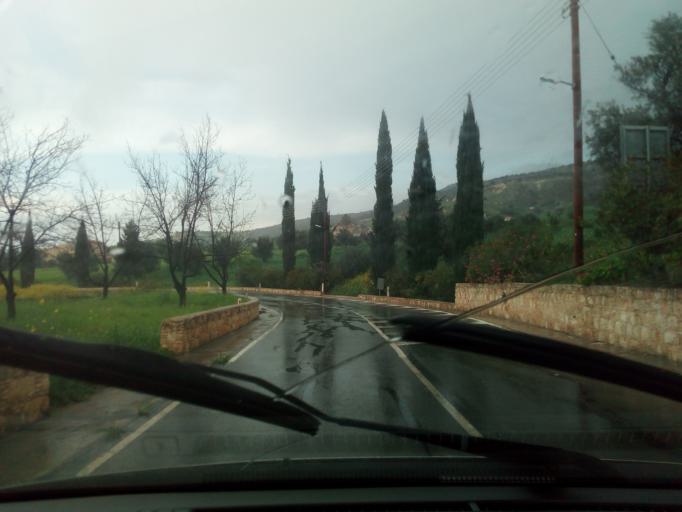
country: CY
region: Pafos
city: Polis
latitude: 35.0006
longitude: 32.4693
